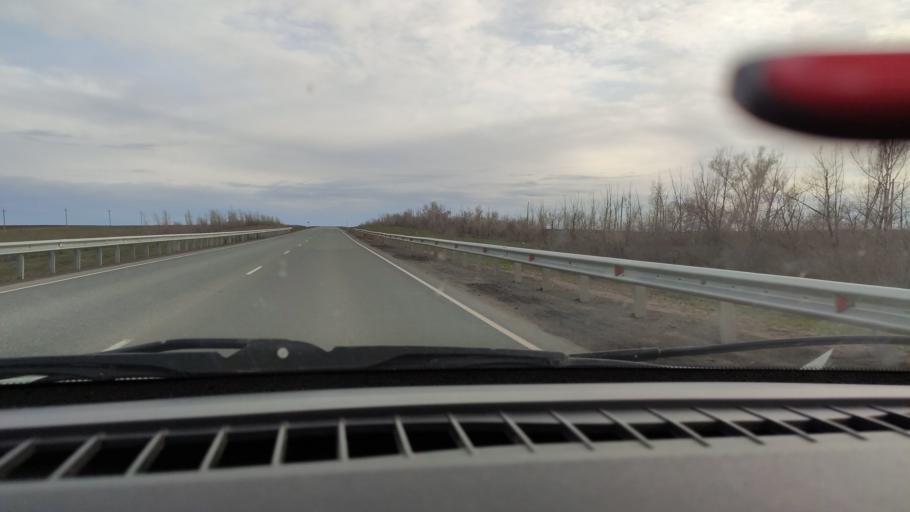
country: RU
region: Orenburg
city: Sakmara
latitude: 52.0746
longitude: 55.2640
